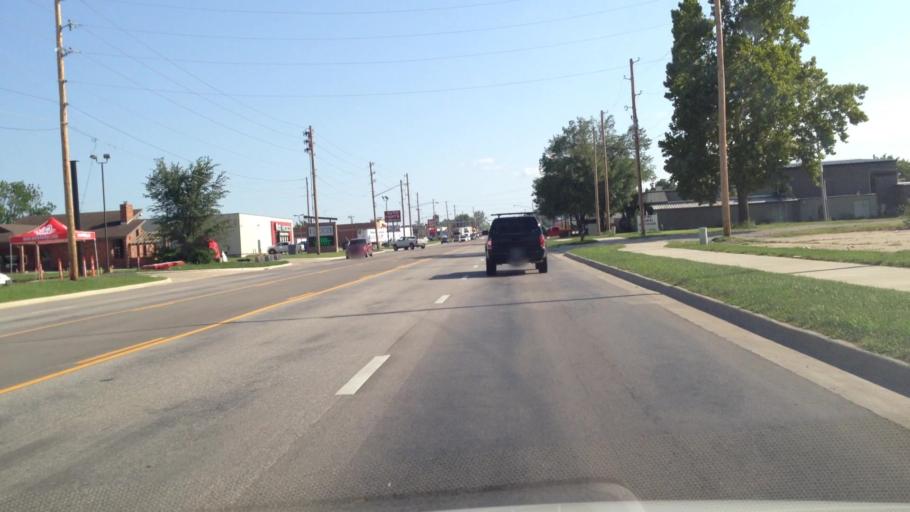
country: US
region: Kansas
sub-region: Bourbon County
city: Fort Scott
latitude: 37.8162
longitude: -94.7056
